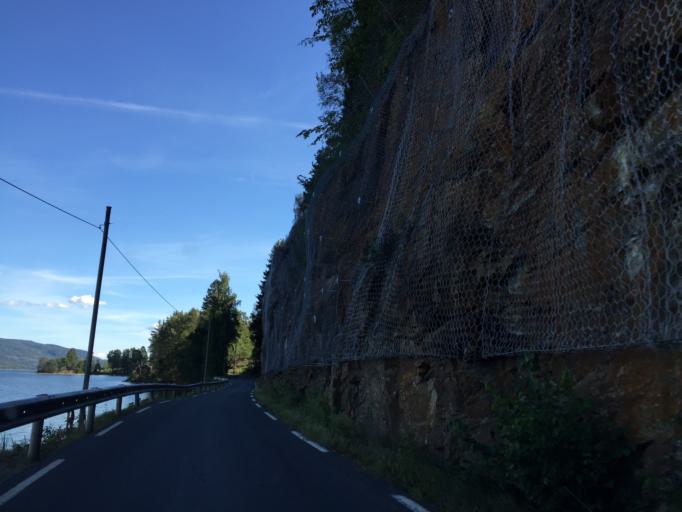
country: NO
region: Buskerud
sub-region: Ovre Eiker
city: Hokksund
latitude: 59.6791
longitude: 9.8622
